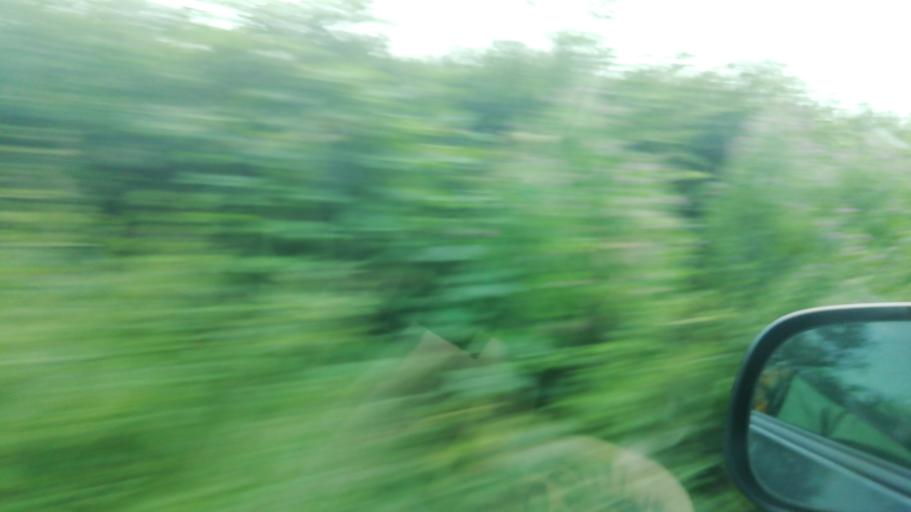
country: IE
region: Munster
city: Fethard
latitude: 52.5337
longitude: -7.6807
